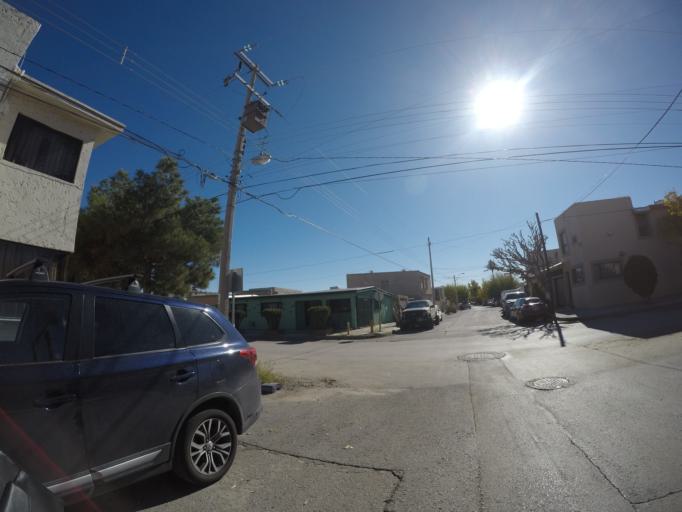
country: MX
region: Chihuahua
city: Ciudad Juarez
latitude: 31.7424
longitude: -106.4608
